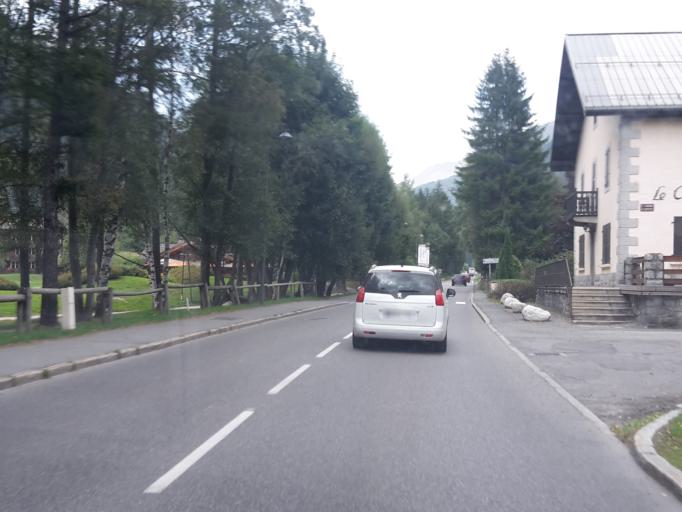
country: FR
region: Rhone-Alpes
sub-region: Departement de la Haute-Savoie
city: Chamonix-Mont-Blanc
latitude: 45.9415
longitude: 6.8876
